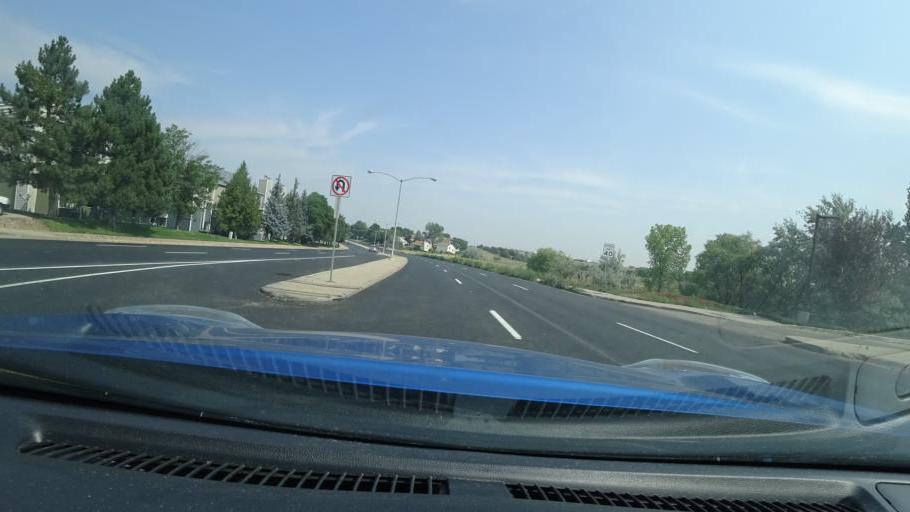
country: US
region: Colorado
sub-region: Adams County
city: Aurora
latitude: 39.6977
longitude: -104.7722
